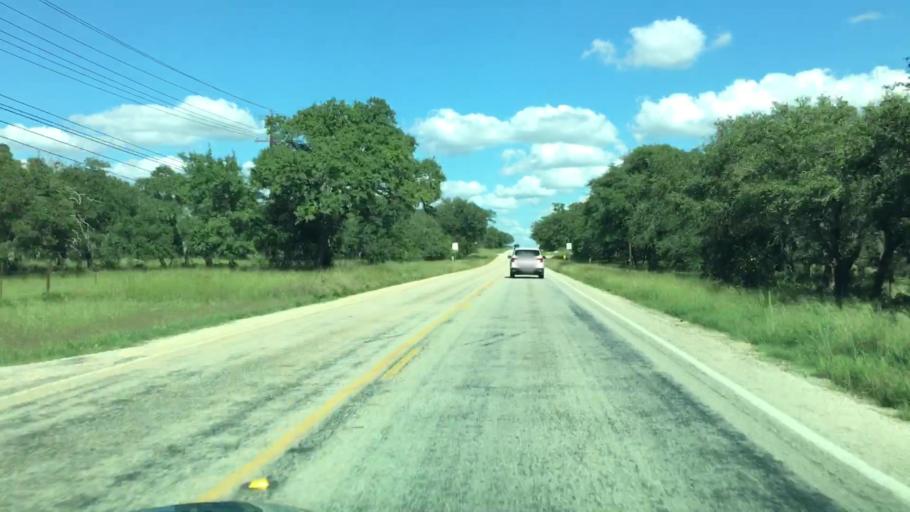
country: US
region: Texas
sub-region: Blanco County
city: Blanco
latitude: 30.0931
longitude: -98.3682
